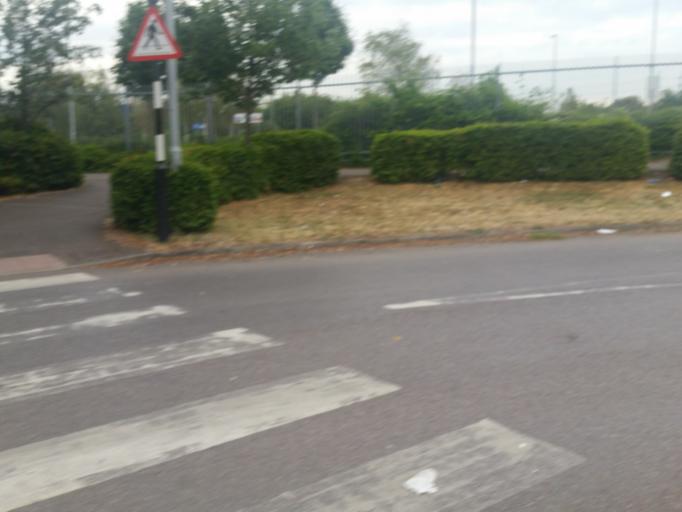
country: GB
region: England
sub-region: Greater London
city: Walthamstow
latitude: 51.6101
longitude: -0.0463
